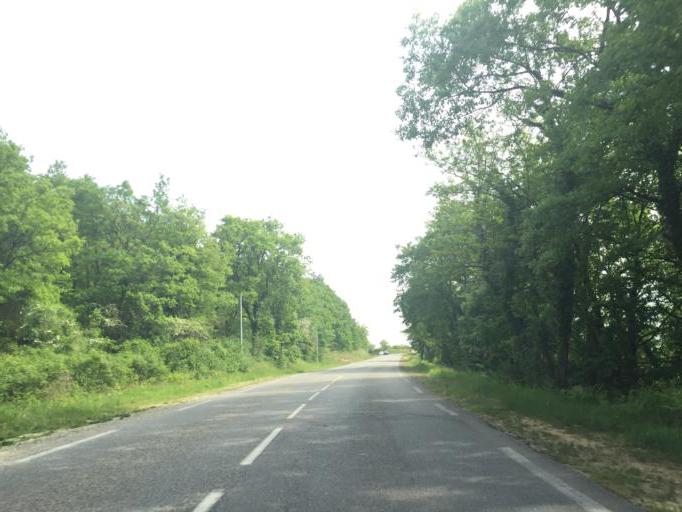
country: FR
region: Rhone-Alpes
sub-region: Departement de la Drome
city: Clerieux
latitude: 45.1306
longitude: 4.9543
